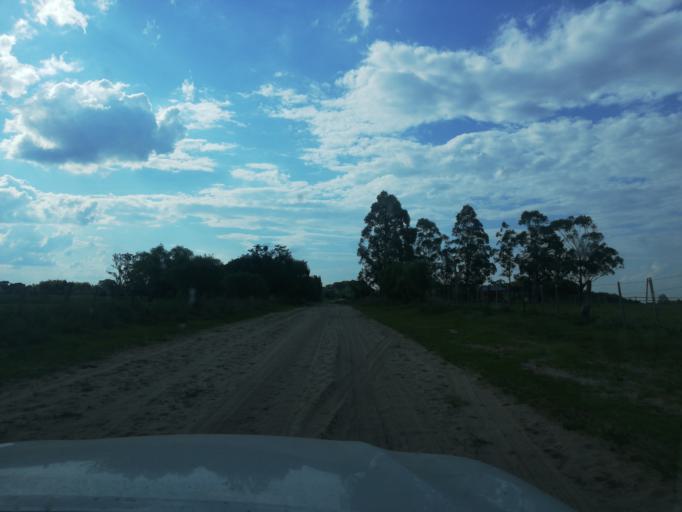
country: AR
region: Corrientes
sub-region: Departamento de San Miguel
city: San Miguel
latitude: -27.9939
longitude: -57.5738
